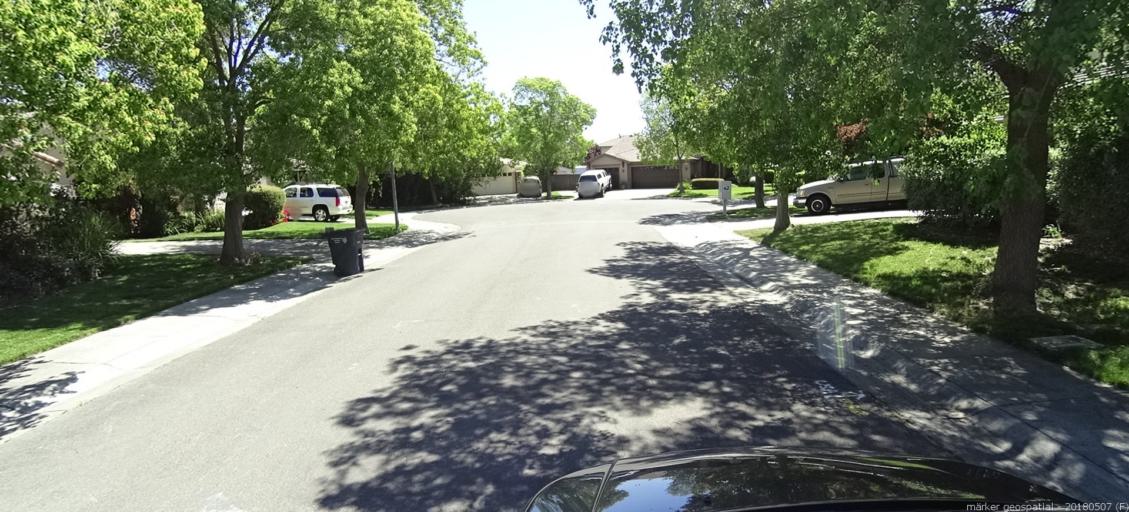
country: US
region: California
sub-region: Sacramento County
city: Rio Linda
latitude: 38.6676
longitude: -121.5104
